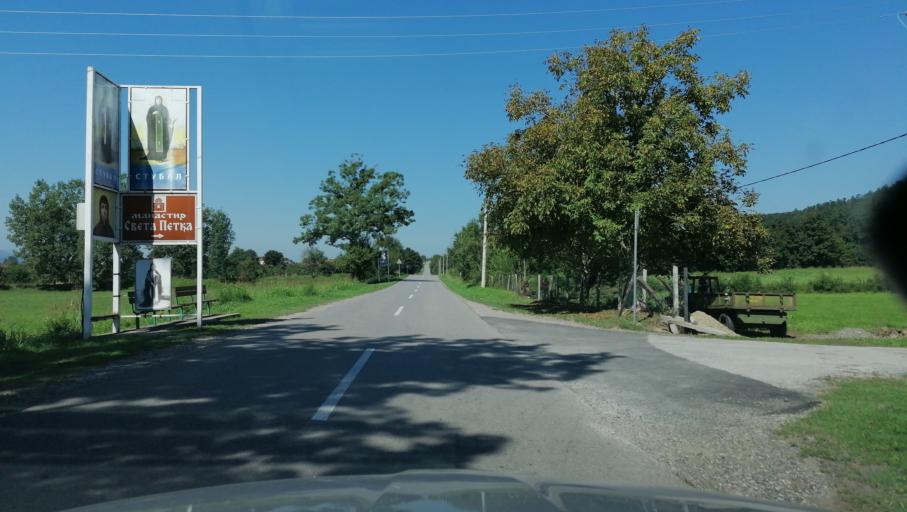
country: RS
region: Central Serbia
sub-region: Raski Okrug
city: Vrnjacka Banja
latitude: 43.6833
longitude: 20.8874
